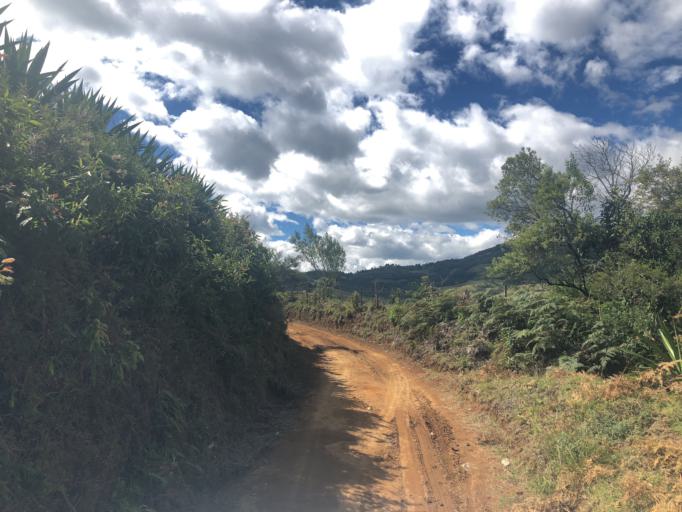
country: CO
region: Cauca
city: Silvia
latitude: 2.6788
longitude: -76.4423
